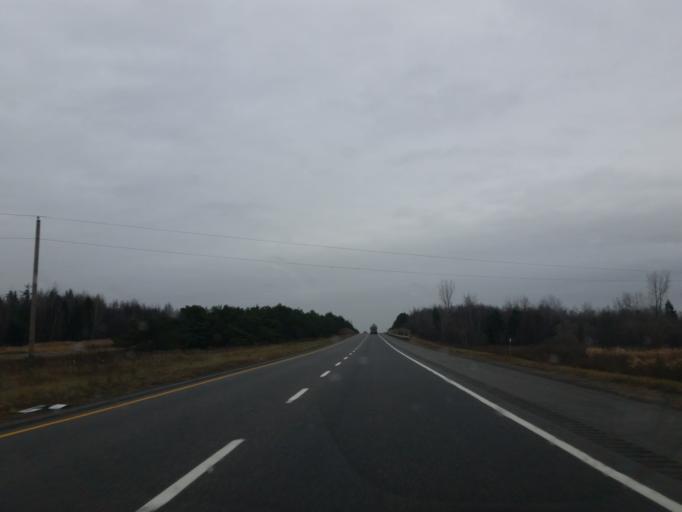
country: CA
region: Quebec
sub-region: Mauricie
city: Becancour
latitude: 46.5232
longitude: -72.2861
